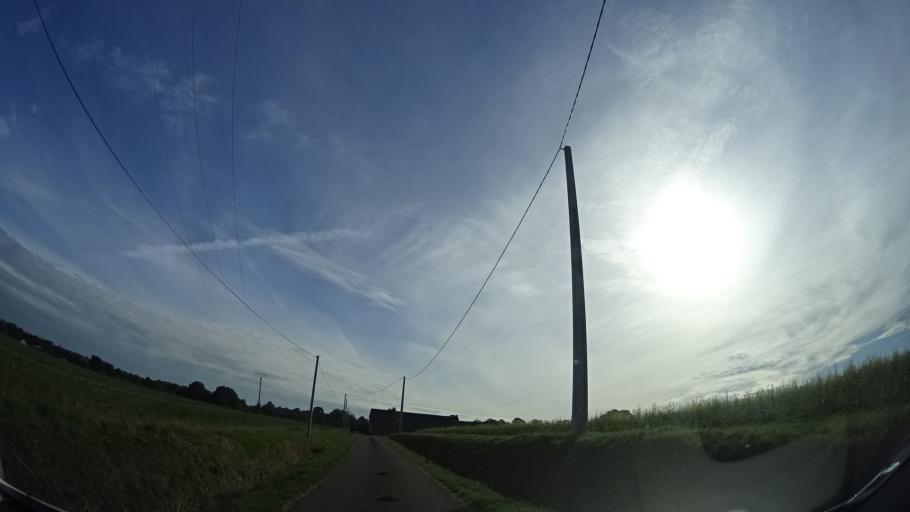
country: FR
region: Brittany
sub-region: Departement d'Ille-et-Vilaine
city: Geveze
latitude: 48.2385
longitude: -1.8291
